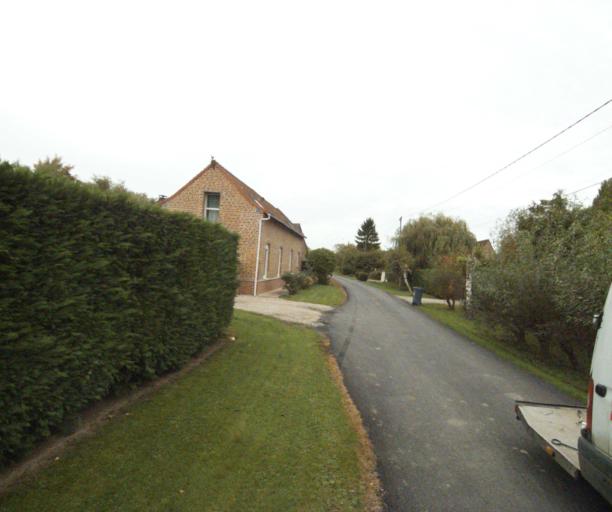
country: FR
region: Nord-Pas-de-Calais
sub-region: Departement du Nord
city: Aubers
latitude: 50.5903
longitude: 2.8117
